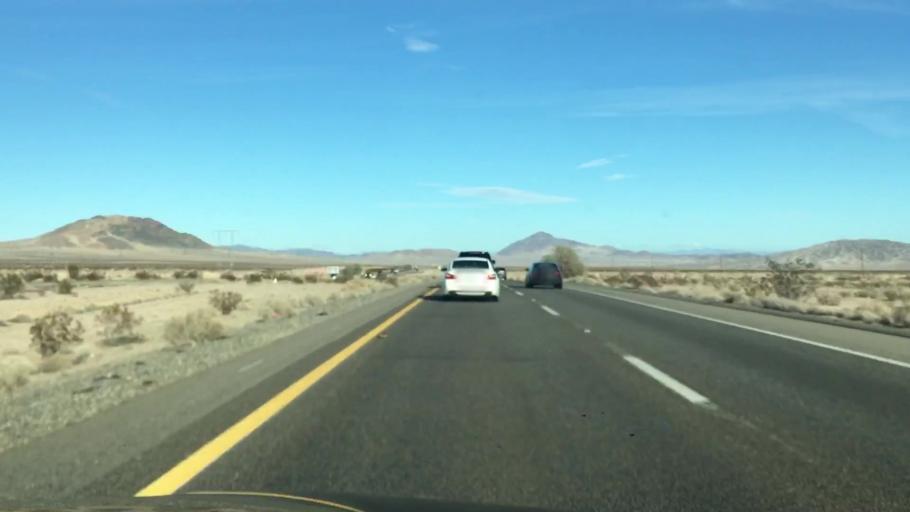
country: US
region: California
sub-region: San Bernardino County
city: Fort Irwin
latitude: 35.0174
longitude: -116.5153
